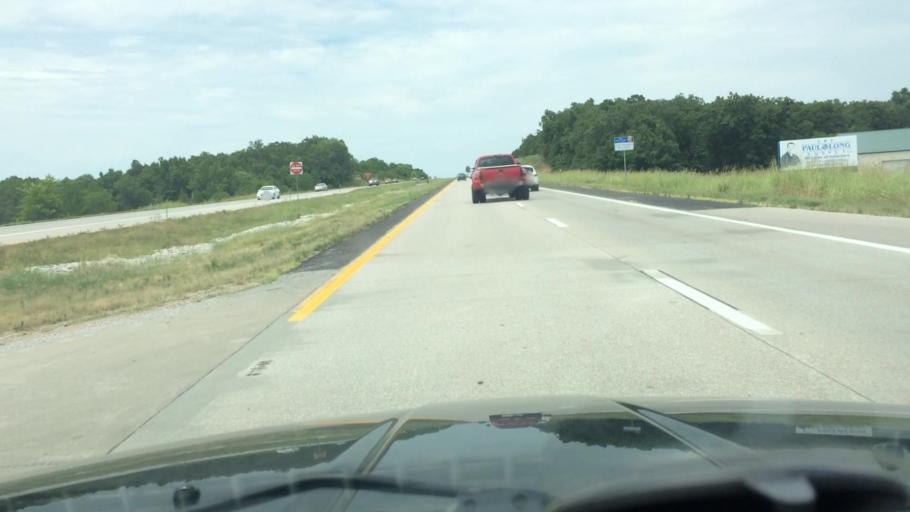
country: US
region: Missouri
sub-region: Greene County
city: Willard
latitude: 37.4362
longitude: -93.3556
